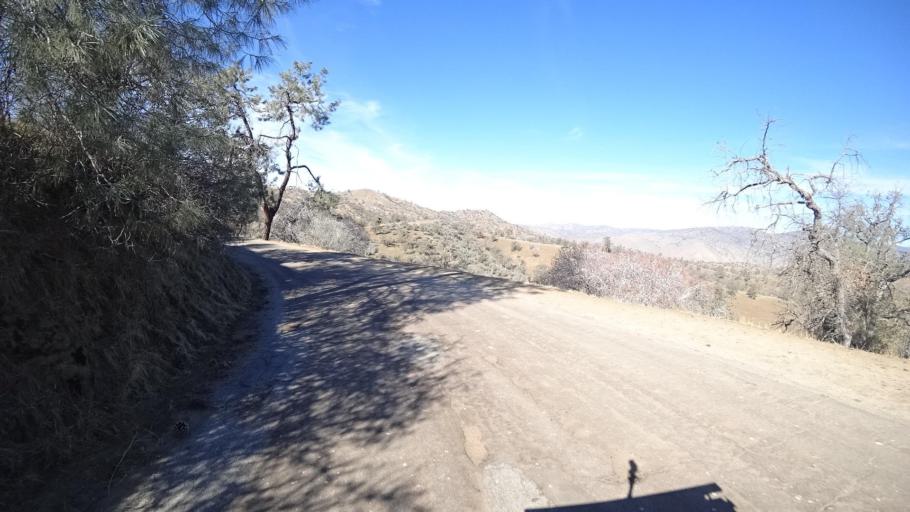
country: US
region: California
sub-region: Kern County
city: Bodfish
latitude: 35.4425
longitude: -118.7074
